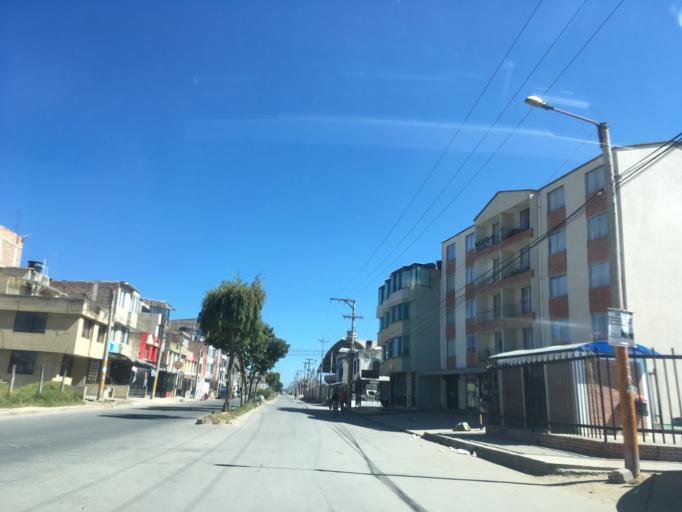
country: CO
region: Boyaca
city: Sogamoso
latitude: 5.7044
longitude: -72.9398
